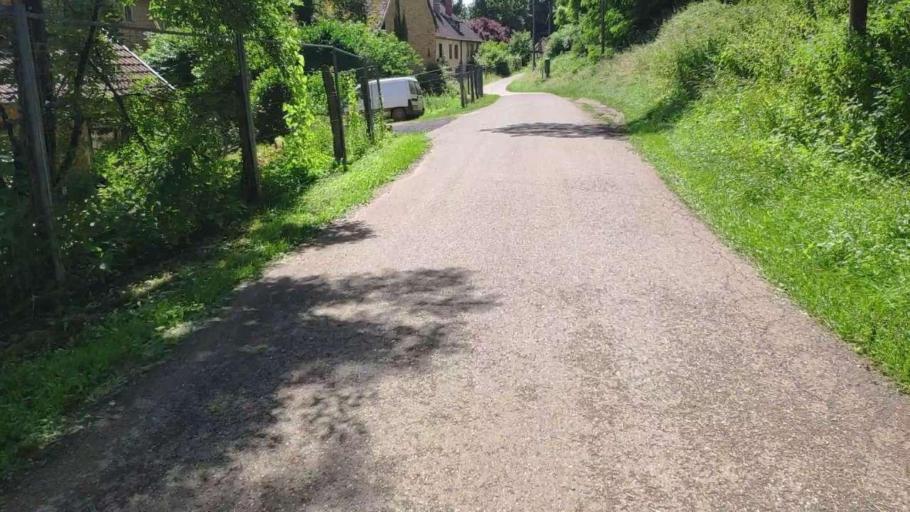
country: FR
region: Franche-Comte
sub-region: Departement du Jura
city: Poligny
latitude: 46.8242
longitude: 5.5727
